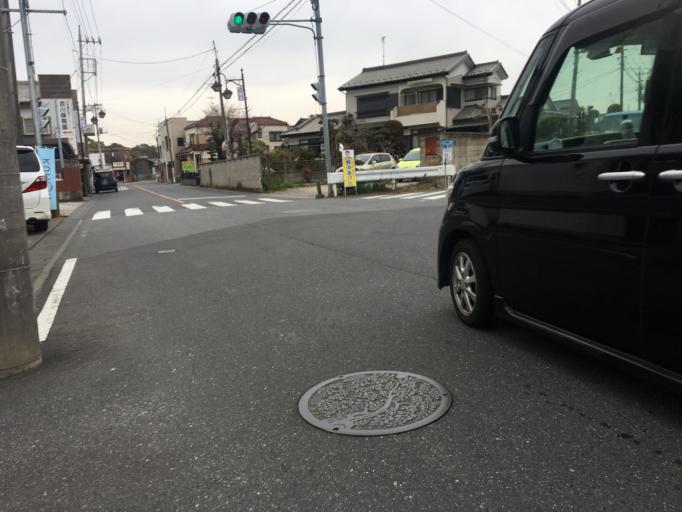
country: JP
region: Saitama
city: Kisai
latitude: 36.1045
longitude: 139.5728
